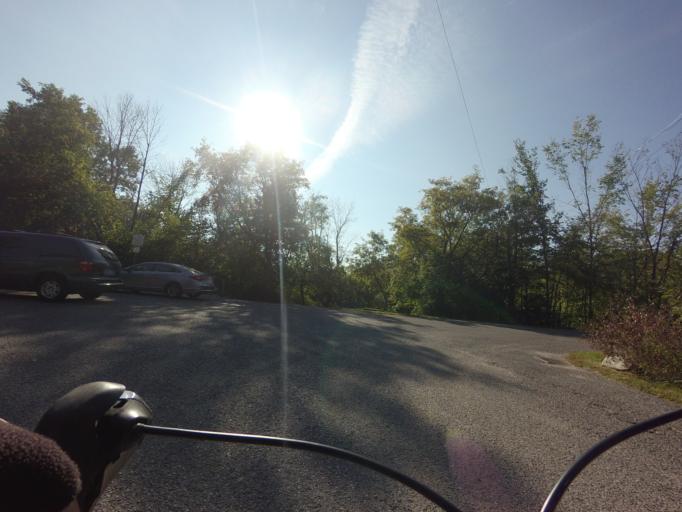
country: CA
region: Ontario
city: Bells Corners
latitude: 45.2284
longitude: -75.6823
